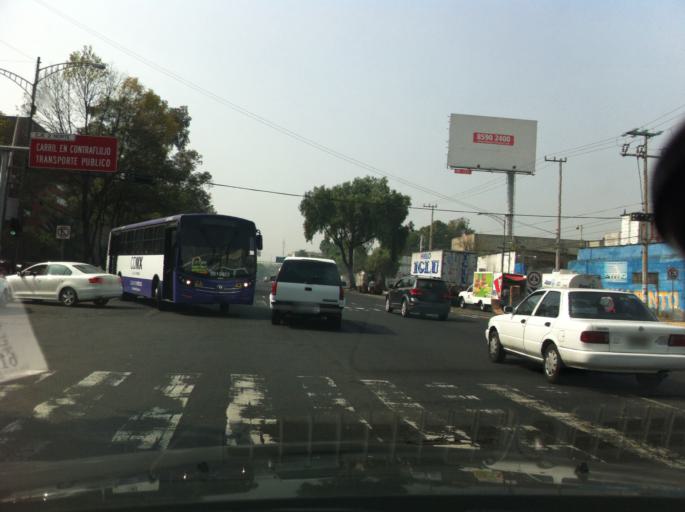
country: MX
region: Mexico City
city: Cuauhtemoc
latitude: 19.4552
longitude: -99.1402
